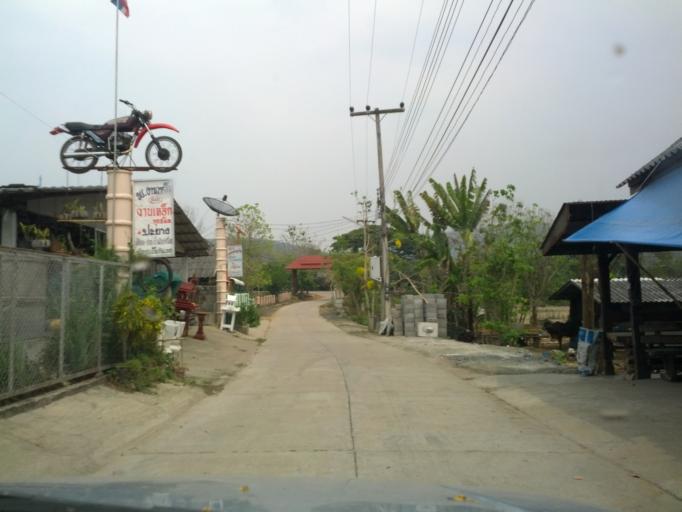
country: TH
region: Chiang Mai
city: Mae Taeng
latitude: 19.1029
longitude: 98.9987
